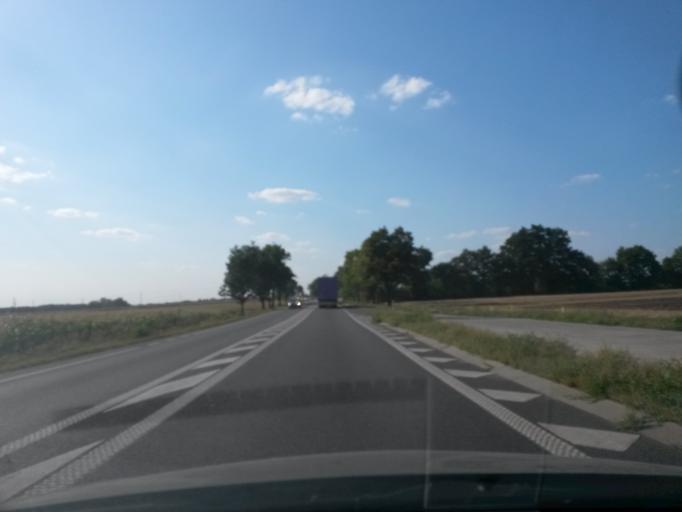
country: PL
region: Masovian Voivodeship
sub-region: Powiat sierpecki
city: Rosciszewo
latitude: 52.8327
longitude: 19.7476
